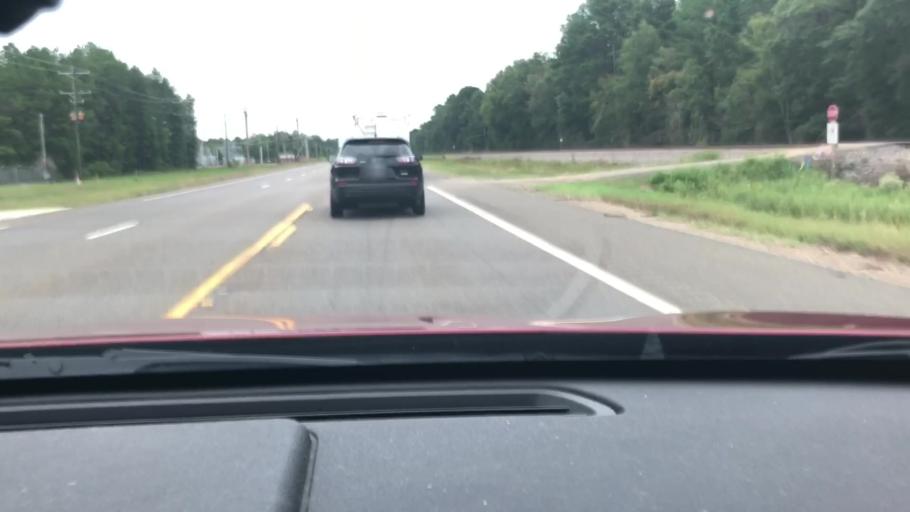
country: US
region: Arkansas
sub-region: Lafayette County
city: Lewisville
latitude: 33.3579
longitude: -93.6026
